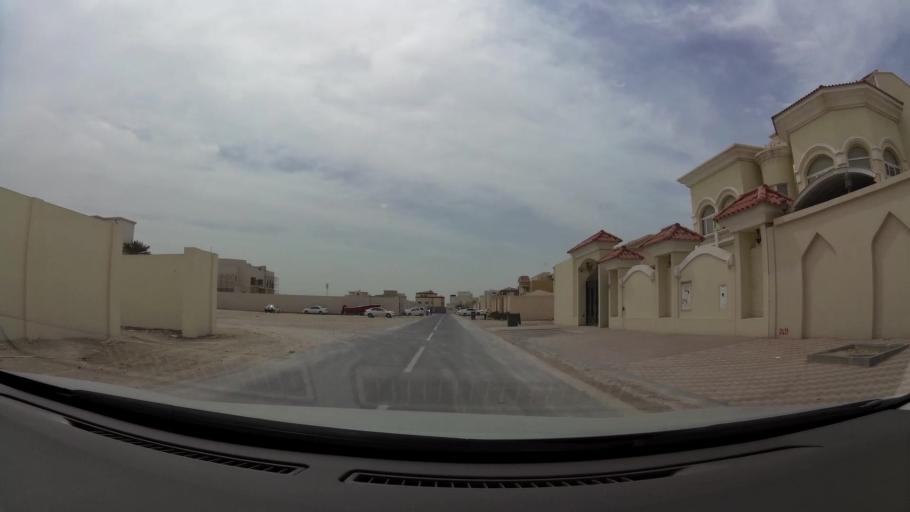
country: QA
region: Baladiyat ad Dawhah
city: Doha
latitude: 25.2191
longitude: 51.4661
